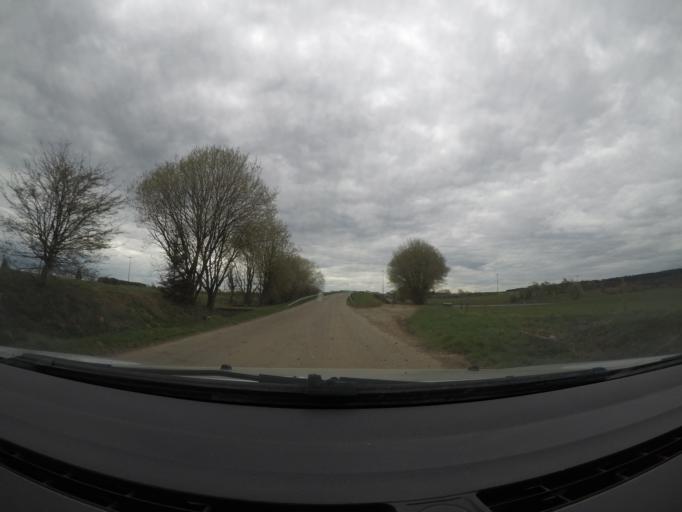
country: BE
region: Wallonia
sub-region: Province du Luxembourg
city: Leglise
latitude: 49.7752
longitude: 5.5430
